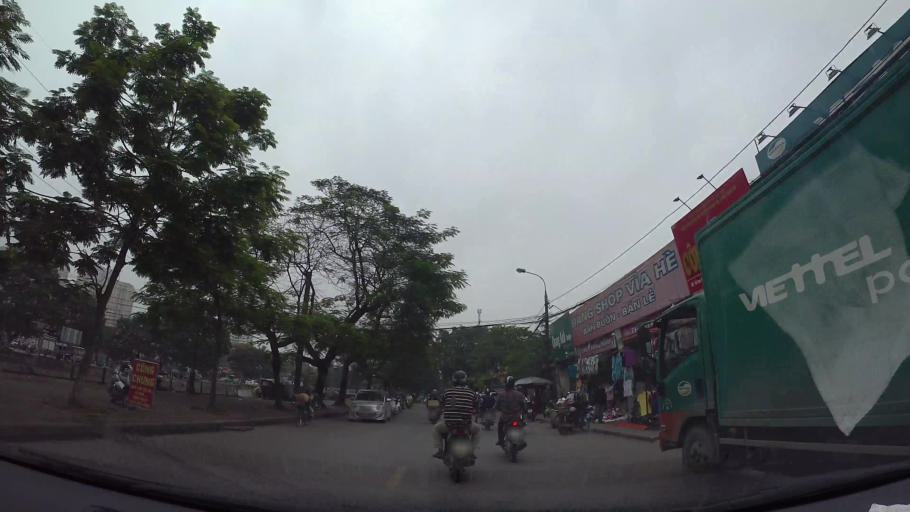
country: VN
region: Ha Noi
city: Hai BaTrung
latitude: 20.9921
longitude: 105.8625
